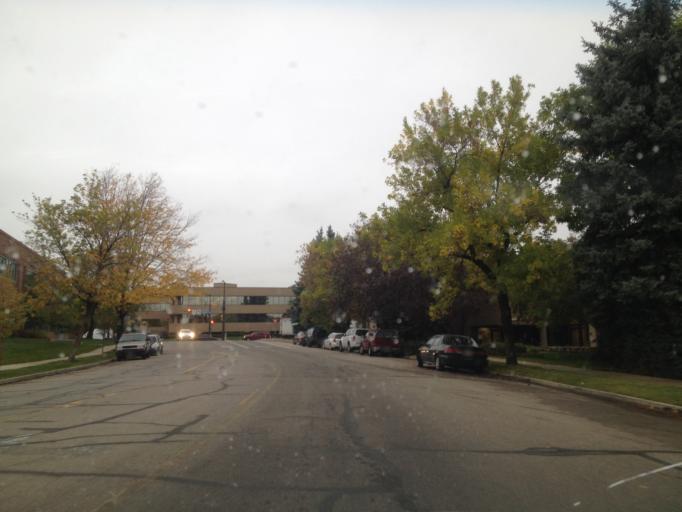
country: US
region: Colorado
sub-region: Boulder County
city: Boulder
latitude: 40.0281
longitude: -105.2476
